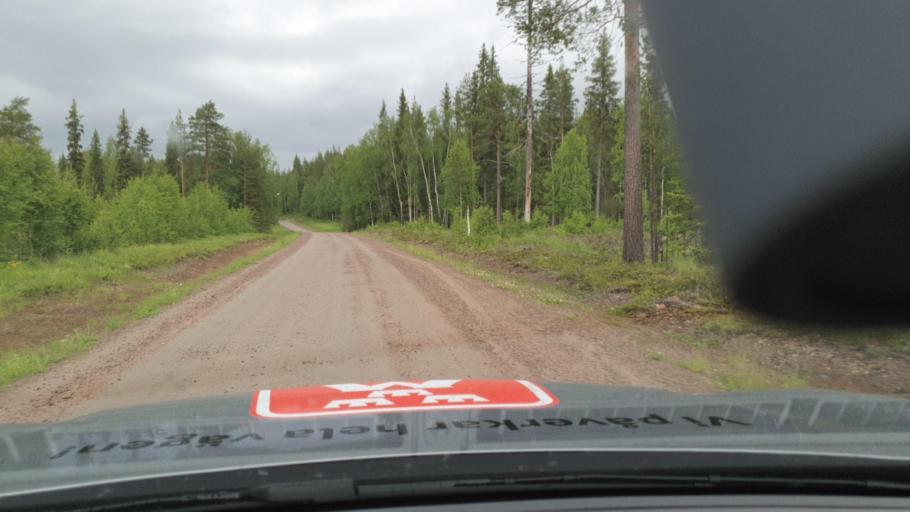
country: SE
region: Norrbotten
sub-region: Overkalix Kommun
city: OEverkalix
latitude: 66.6249
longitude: 22.7244
